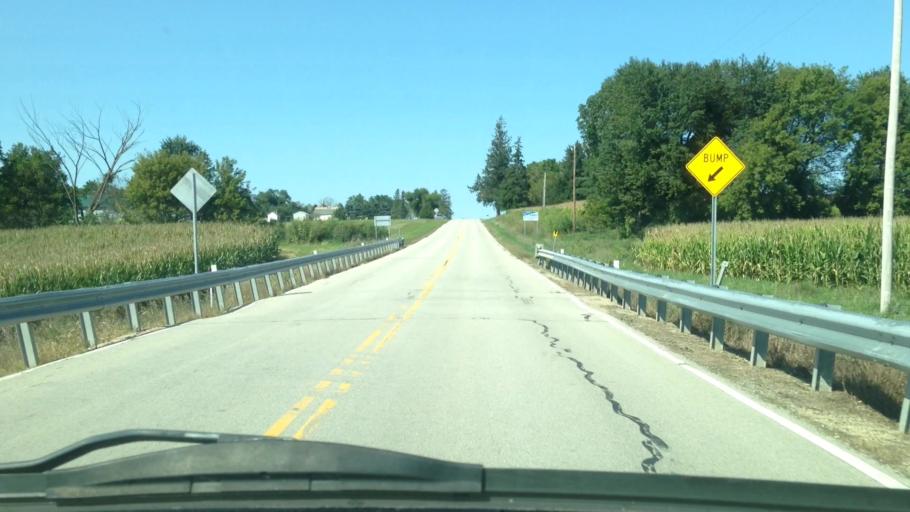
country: US
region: Minnesota
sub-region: Fillmore County
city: Rushford
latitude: 43.7051
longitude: -91.7704
